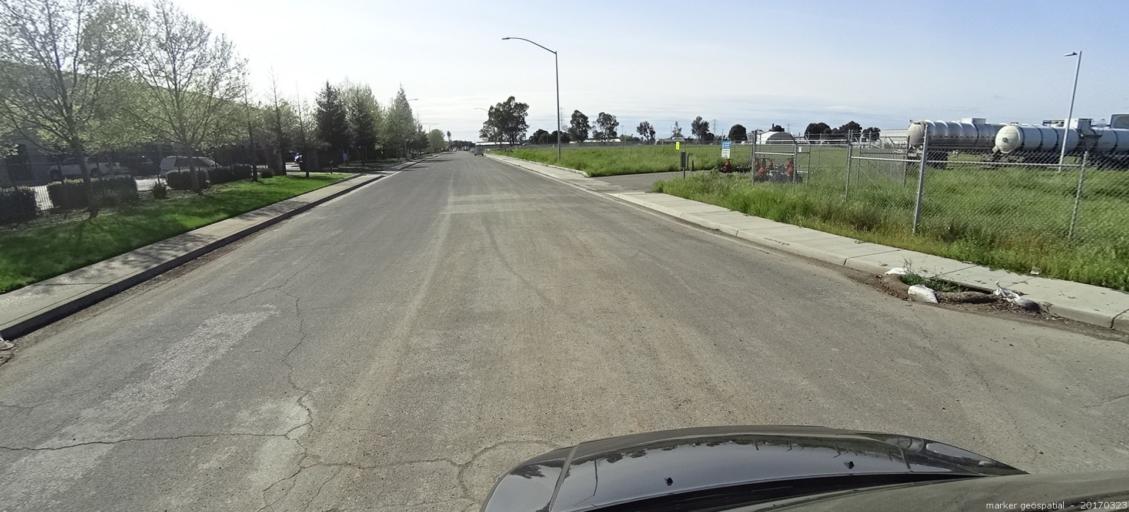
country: US
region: California
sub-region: Sacramento County
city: Rosemont
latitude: 38.5215
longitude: -121.3826
